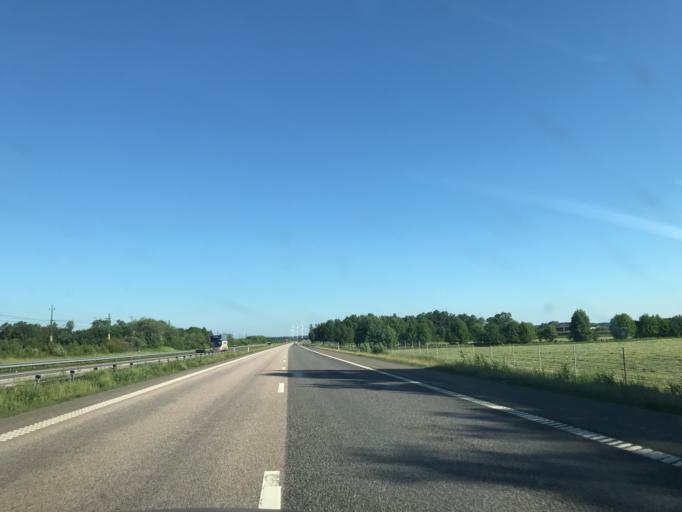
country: SE
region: Halland
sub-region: Varbergs Kommun
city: Tvaaker
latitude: 57.0035
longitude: 12.4041
